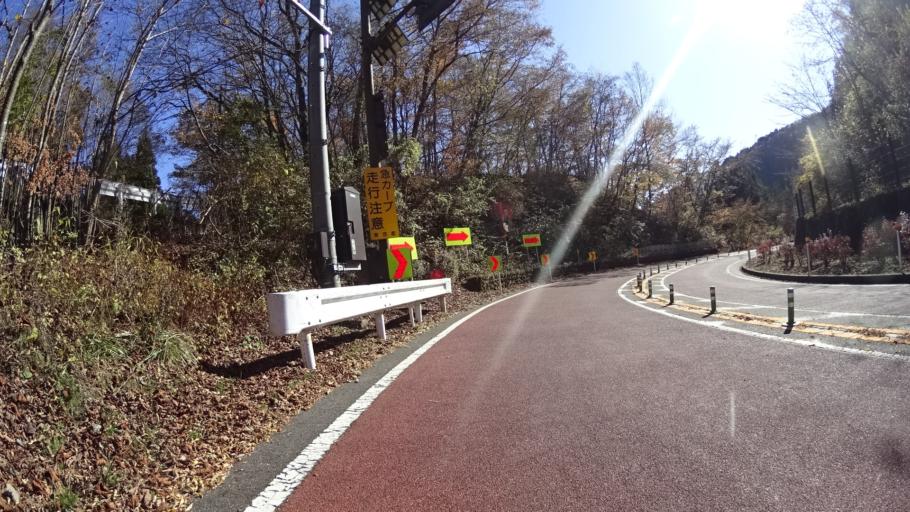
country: JP
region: Yamanashi
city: Uenohara
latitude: 35.7467
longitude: 139.0425
